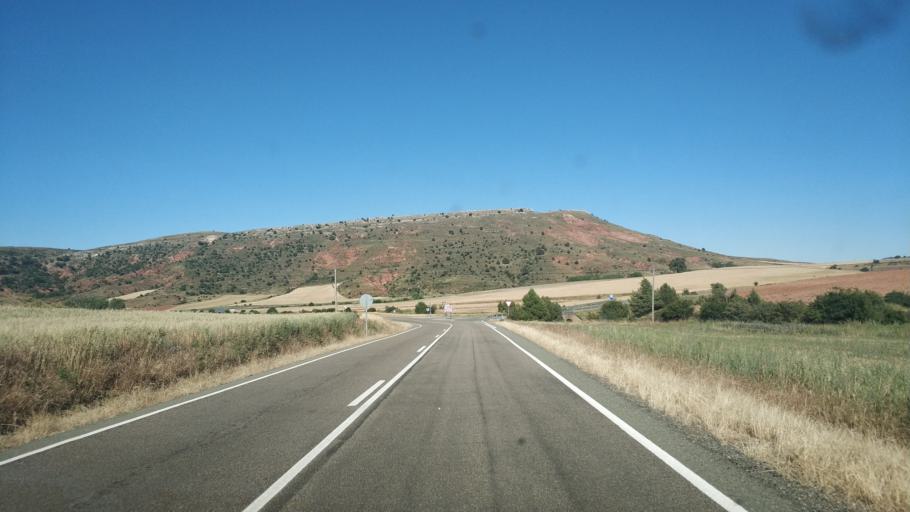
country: ES
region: Castille and Leon
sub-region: Provincia de Soria
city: Montejo de Tiermes
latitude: 41.3467
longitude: -3.1504
